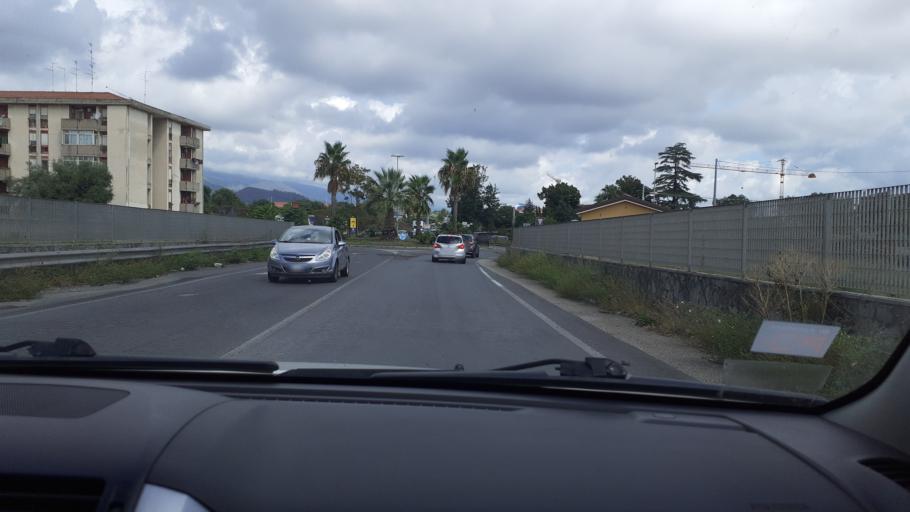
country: IT
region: Sicily
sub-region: Catania
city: San Giovanni la Punta
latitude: 37.5774
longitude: 15.1036
